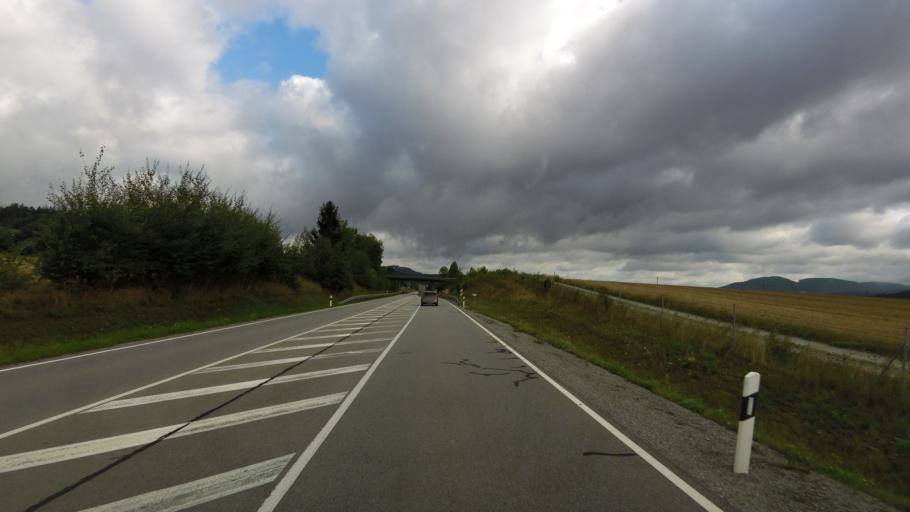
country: DE
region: Bavaria
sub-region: Lower Bavaria
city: Ascha
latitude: 48.9903
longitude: 12.6309
